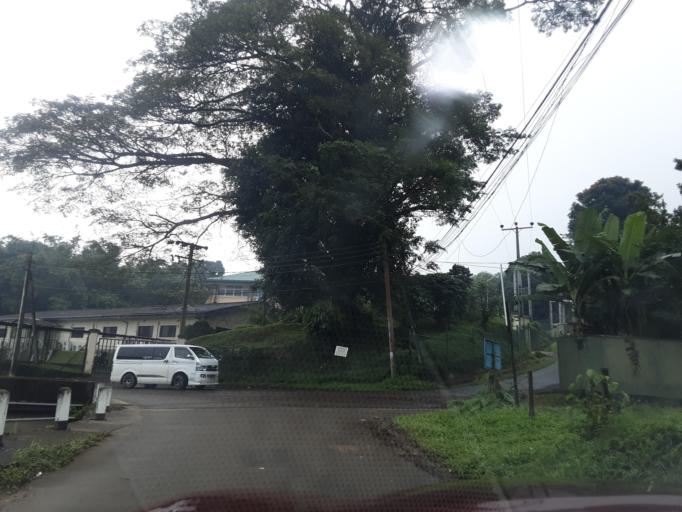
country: LK
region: Central
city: Kandy
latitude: 7.3183
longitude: 80.6215
